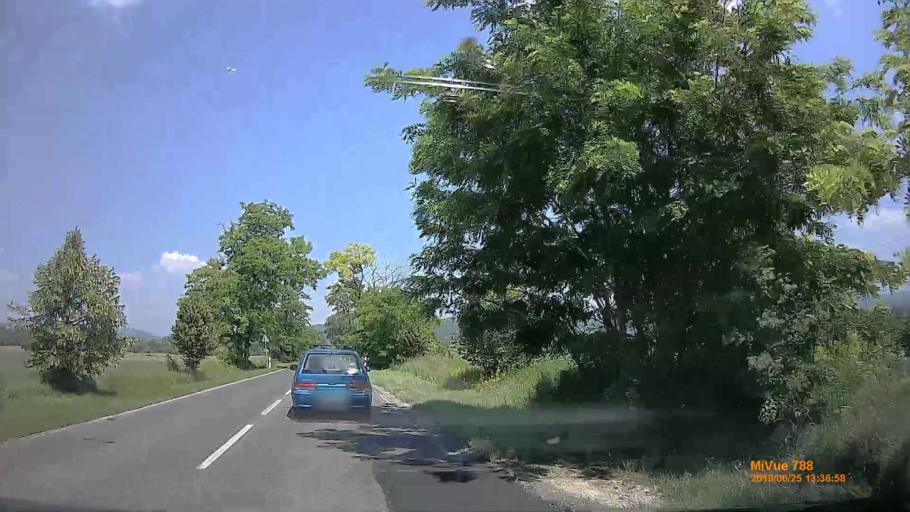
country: SK
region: Nitriansky
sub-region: Okres Nove Zamky
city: Sturovo
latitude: 47.7736
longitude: 18.7207
